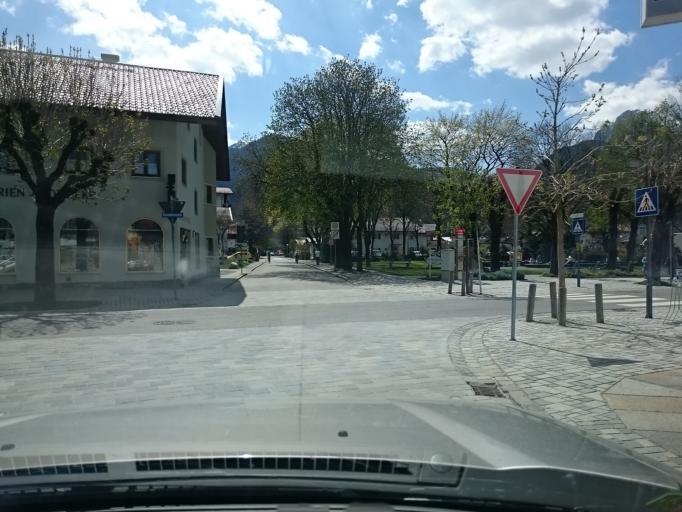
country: DE
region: Bavaria
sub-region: Upper Bavaria
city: Mittenwald
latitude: 47.4413
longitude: 11.2629
